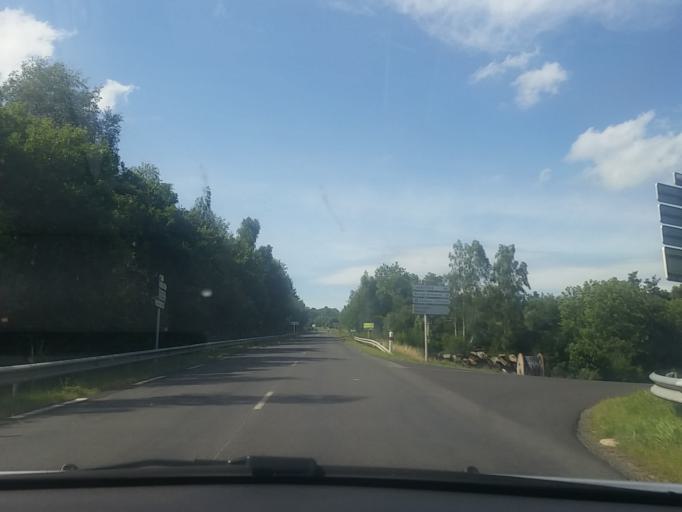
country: FR
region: Auvergne
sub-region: Departement du Cantal
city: Neuveglise
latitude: 44.9258
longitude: 3.0013
